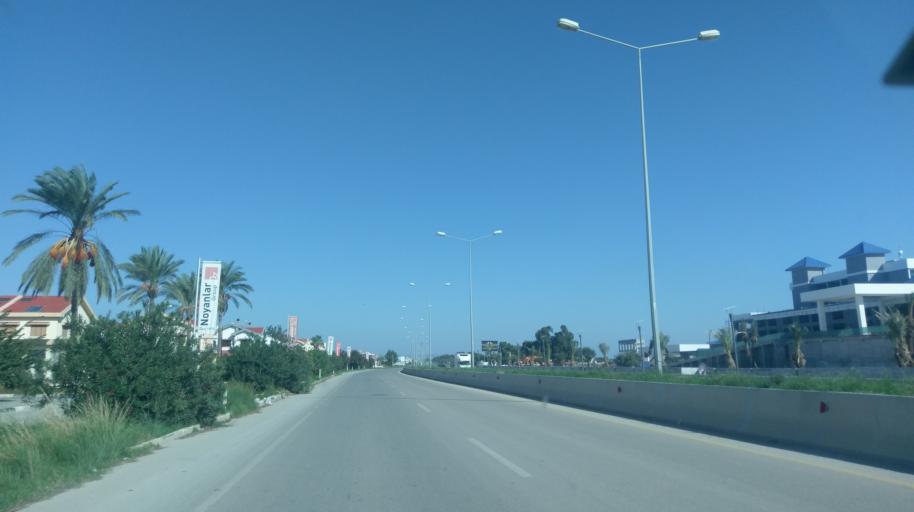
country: CY
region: Ammochostos
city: Trikomo
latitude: 35.2660
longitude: 33.9130
